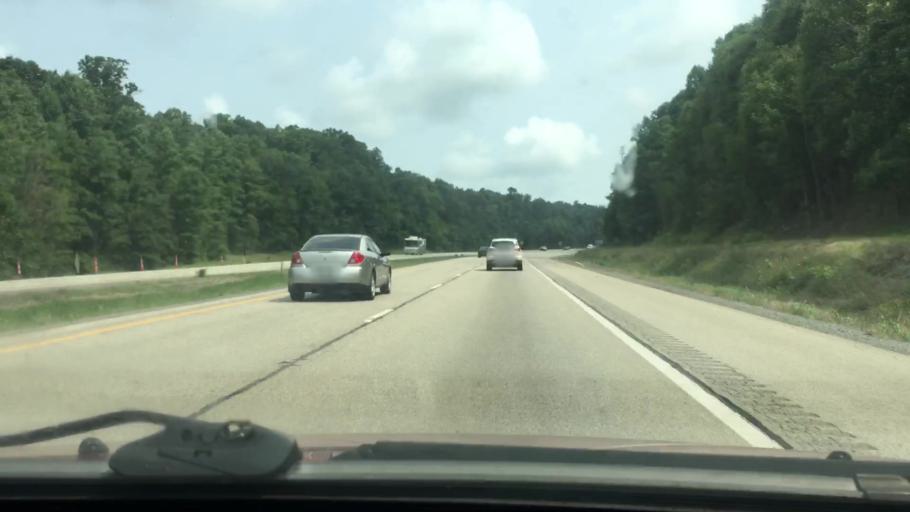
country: US
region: West Virginia
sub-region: Monongalia County
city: Cheat Lake
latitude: 39.6516
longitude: -79.7004
